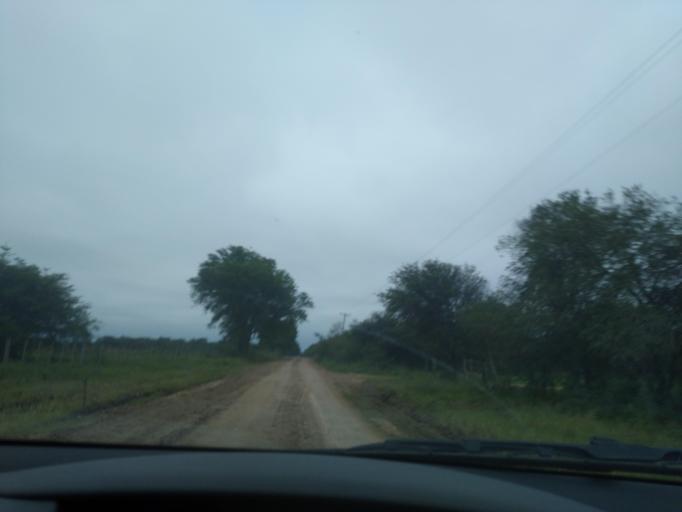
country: AR
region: Chaco
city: Colonia Benitez
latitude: -27.3580
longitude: -58.9619
